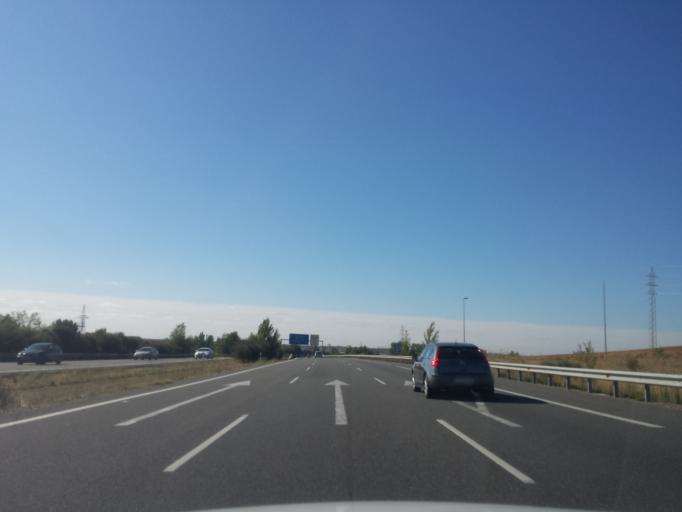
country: ES
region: Castille and Leon
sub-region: Provincia de Zamora
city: Benavente
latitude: 42.0222
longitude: -5.6698
